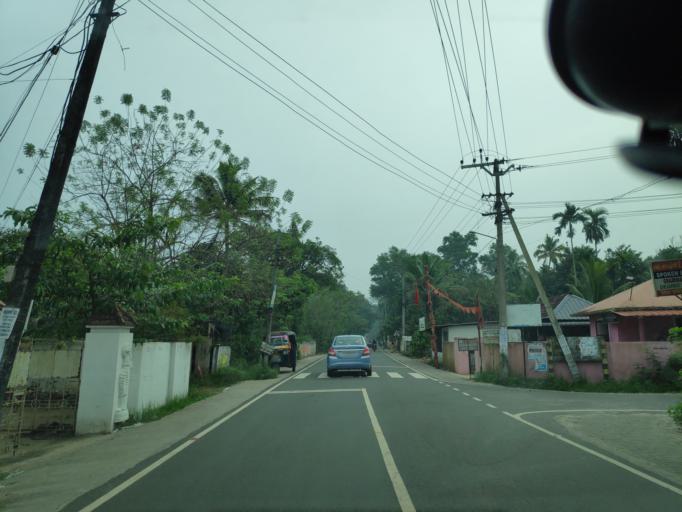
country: IN
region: Kerala
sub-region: Alappuzha
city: Shertallai
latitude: 9.6072
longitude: 76.3526
